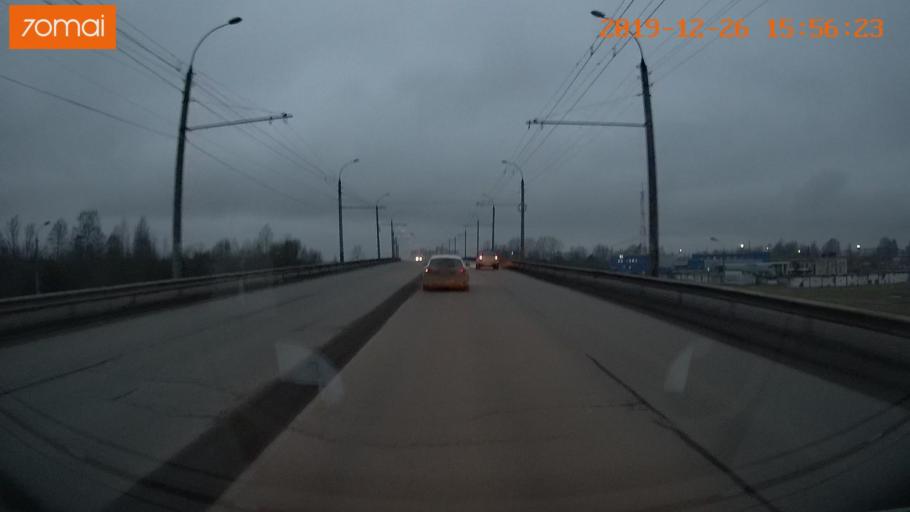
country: RU
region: Jaroslavl
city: Rybinsk
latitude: 58.0430
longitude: 38.8031
